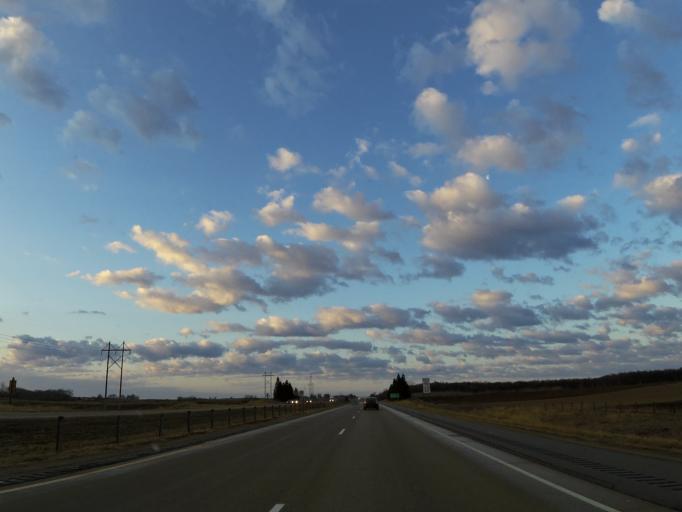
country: US
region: Minnesota
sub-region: Rice County
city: Dundas
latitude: 44.4178
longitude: -93.2928
